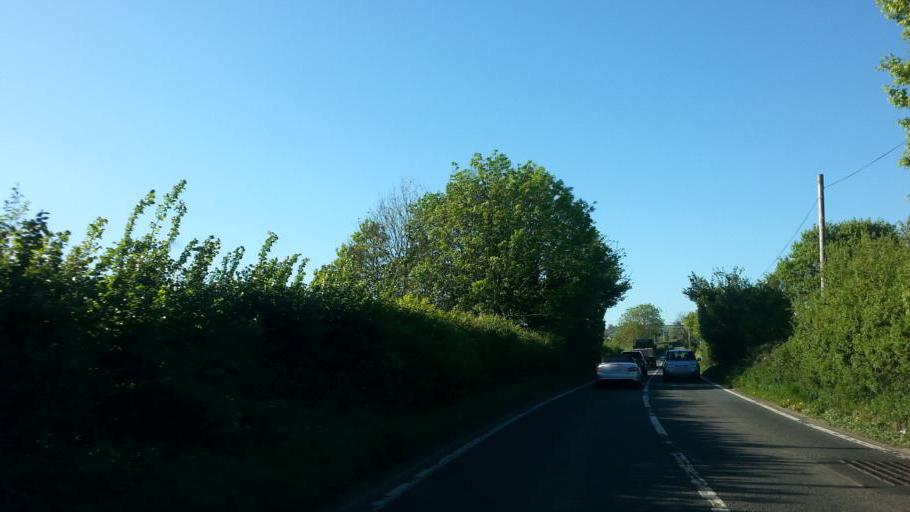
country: GB
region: England
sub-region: Somerset
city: Evercreech
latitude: 51.1450
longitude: -2.5212
